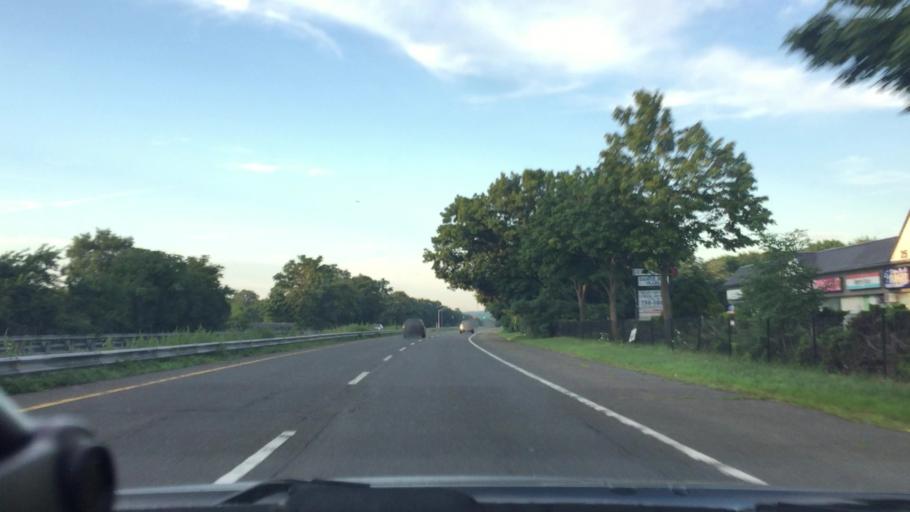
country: US
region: New York
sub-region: Suffolk County
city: Coram
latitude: 40.8952
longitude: -73.0051
